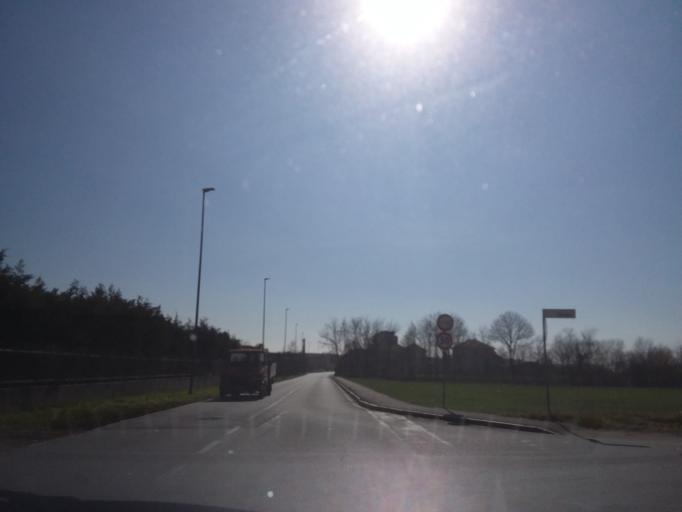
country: IT
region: Piedmont
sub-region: Provincia di Torino
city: Tetti Neirotti
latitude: 45.0615
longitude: 7.5403
